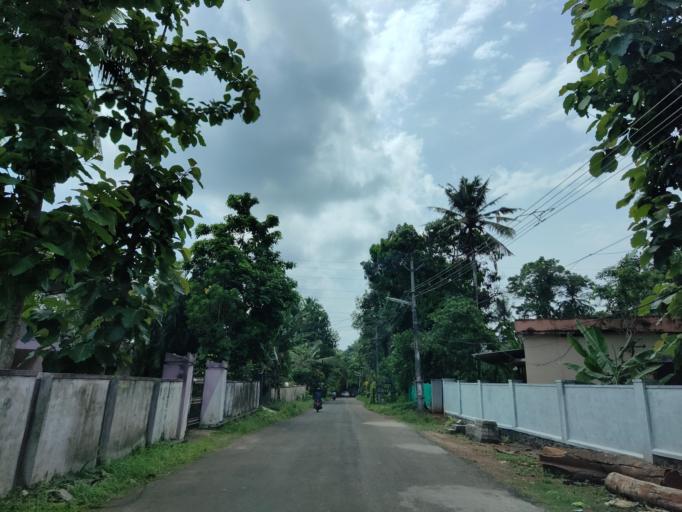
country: IN
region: Kerala
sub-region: Alappuzha
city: Mavelikara
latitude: 9.2540
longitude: 76.5676
